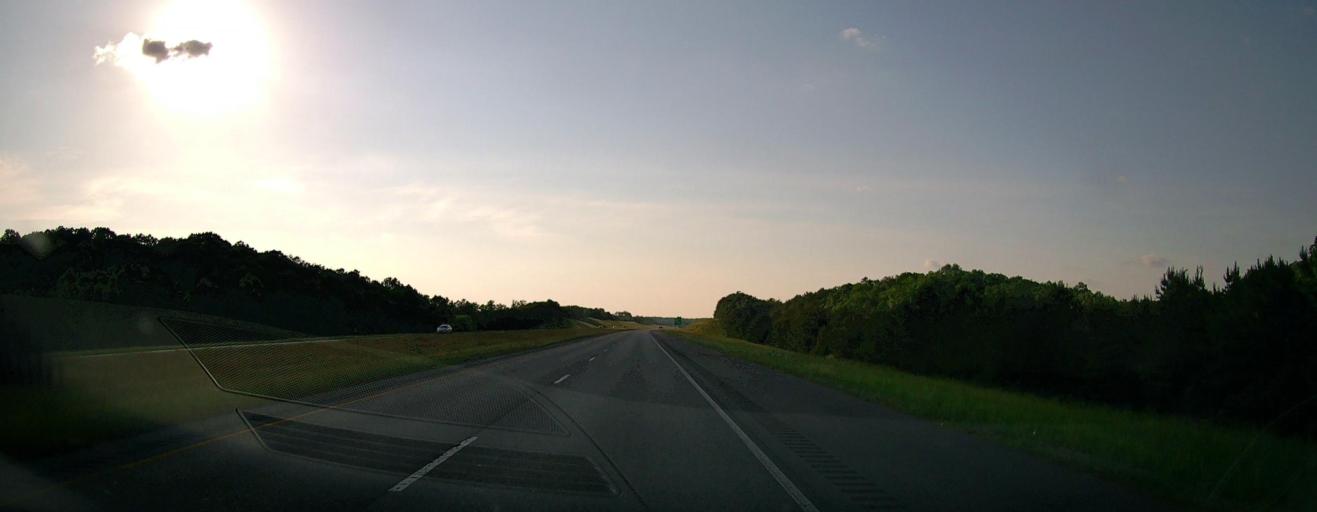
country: US
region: Alabama
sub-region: Walker County
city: Jasper
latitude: 33.8418
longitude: -87.3330
